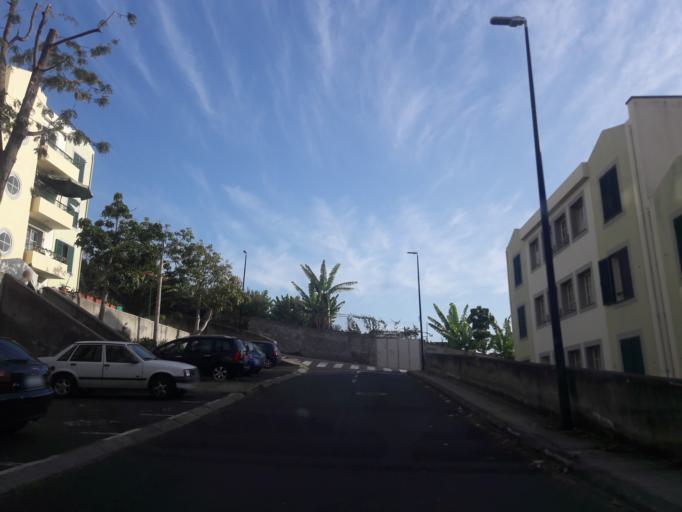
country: PT
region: Madeira
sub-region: Funchal
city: Nossa Senhora do Monte
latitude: 32.6562
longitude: -16.9287
